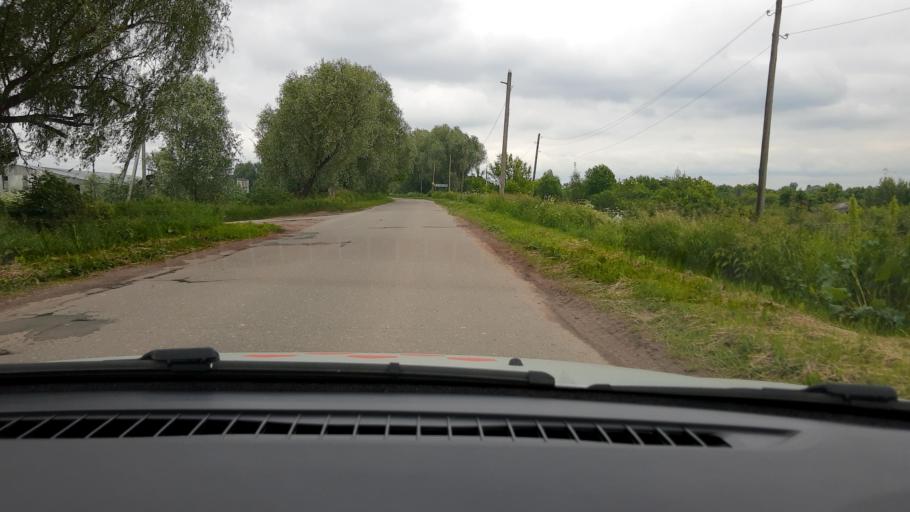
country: RU
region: Nizjnij Novgorod
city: Bogorodsk
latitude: 56.0736
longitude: 43.5084
